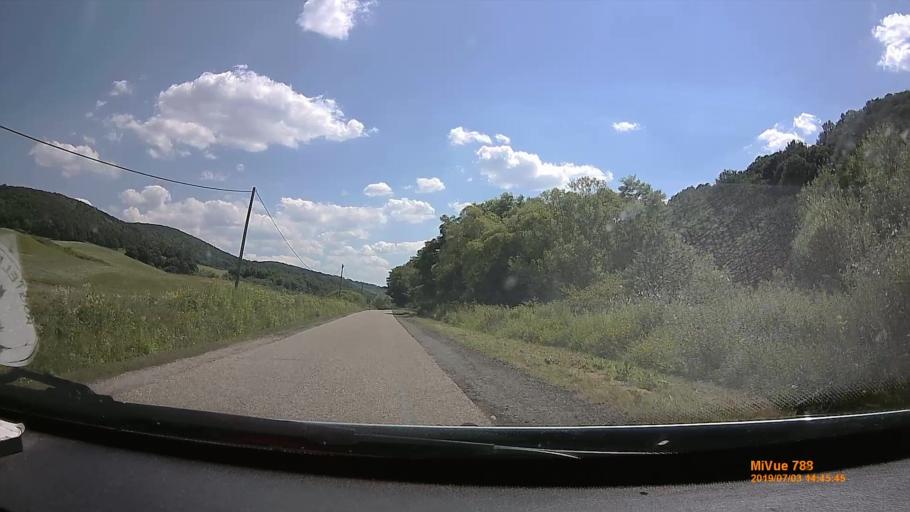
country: HU
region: Borsod-Abauj-Zemplen
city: Putnok
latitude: 48.2601
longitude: 20.4192
